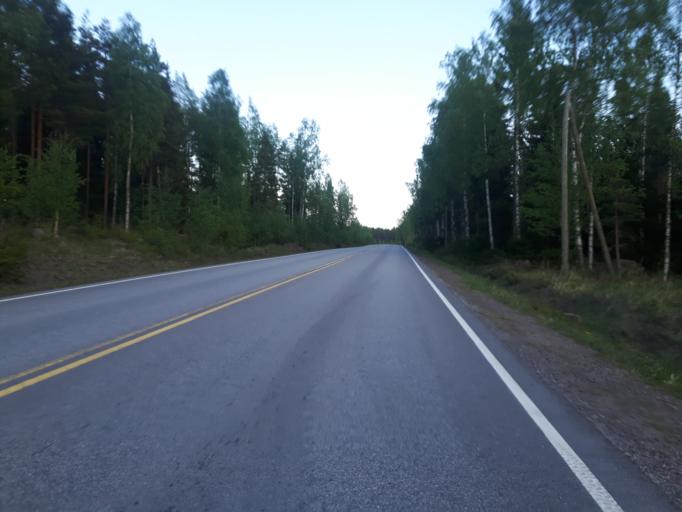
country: FI
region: Uusimaa
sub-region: Loviisa
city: Perna
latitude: 60.4571
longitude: 26.0804
